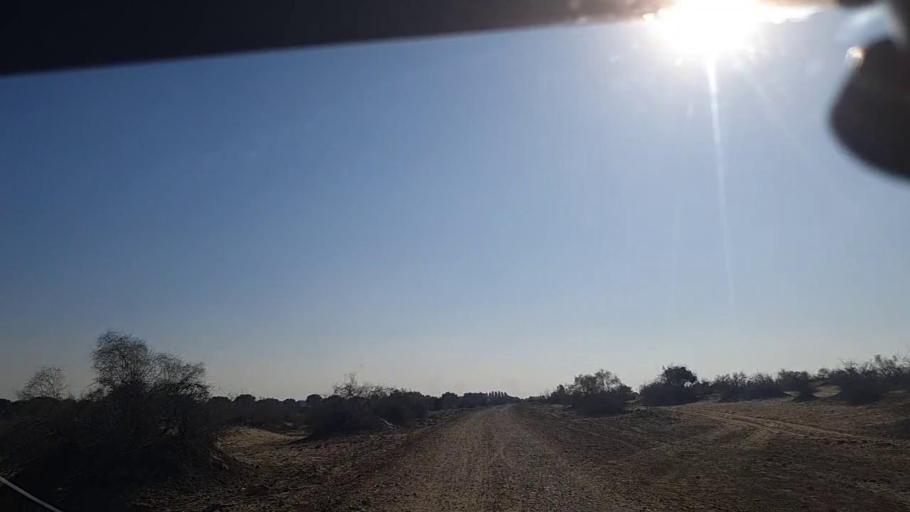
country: PK
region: Sindh
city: Khanpur
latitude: 27.6415
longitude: 69.4057
